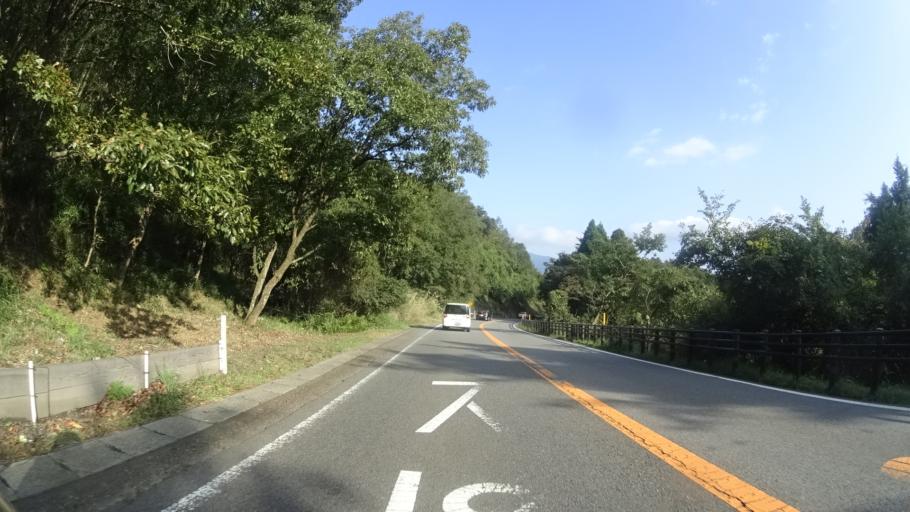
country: JP
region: Oita
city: Tsukawaki
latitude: 33.2534
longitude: 131.3019
